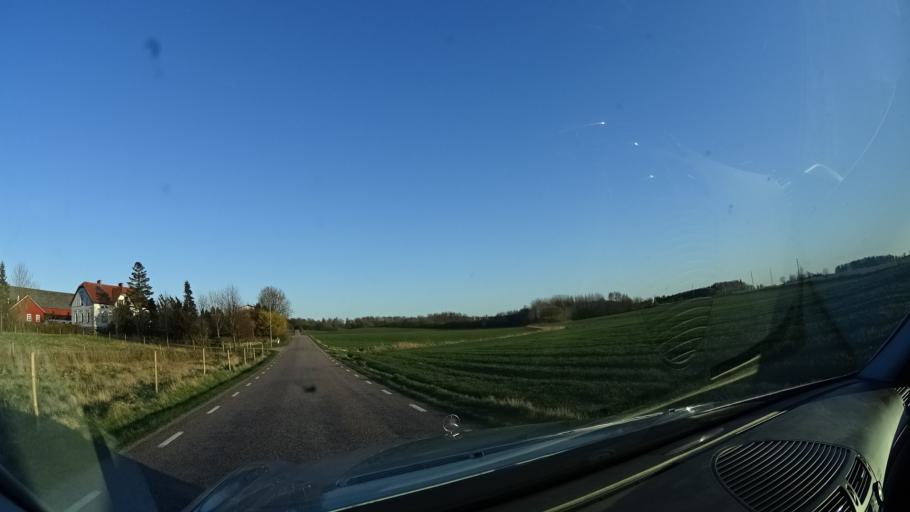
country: SE
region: Skane
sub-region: Klippans Kommun
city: Ljungbyhed
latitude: 55.9614
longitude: 13.2520
